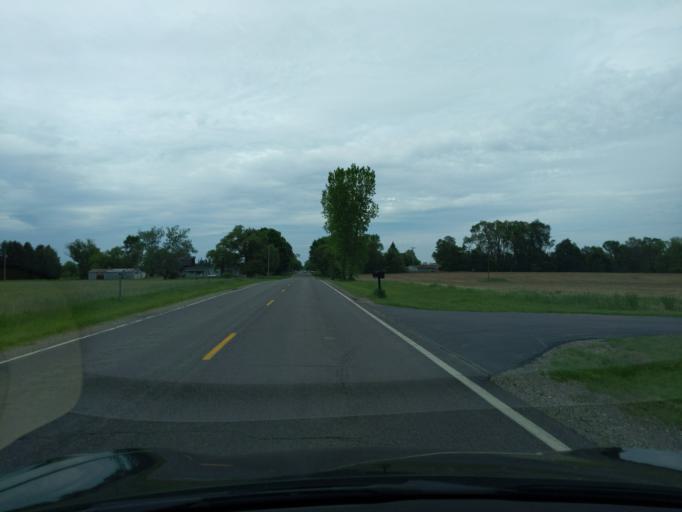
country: US
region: Michigan
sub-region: Ingham County
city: Leslie
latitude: 42.4787
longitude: -84.3561
